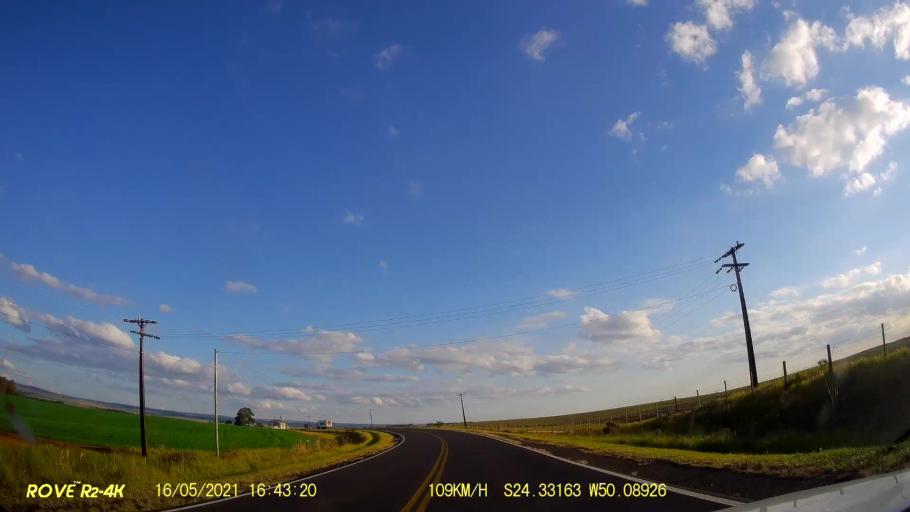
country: BR
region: Parana
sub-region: Pirai Do Sul
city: Pirai do Sul
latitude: -24.3323
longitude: -50.0893
